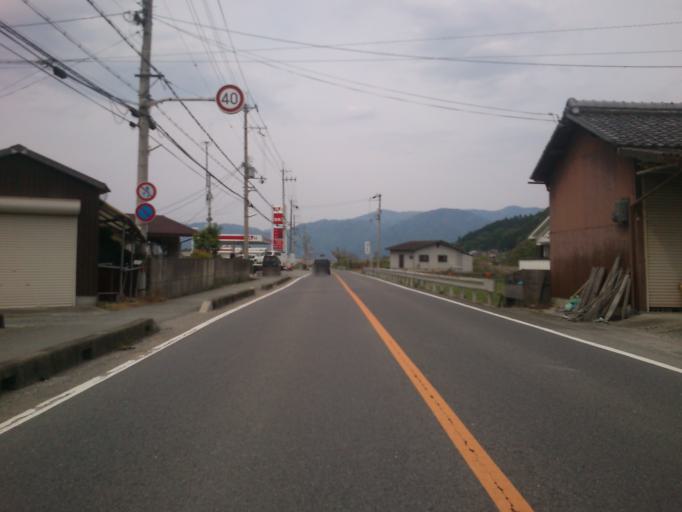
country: JP
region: Kyoto
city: Kameoka
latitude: 34.9999
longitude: 135.5528
